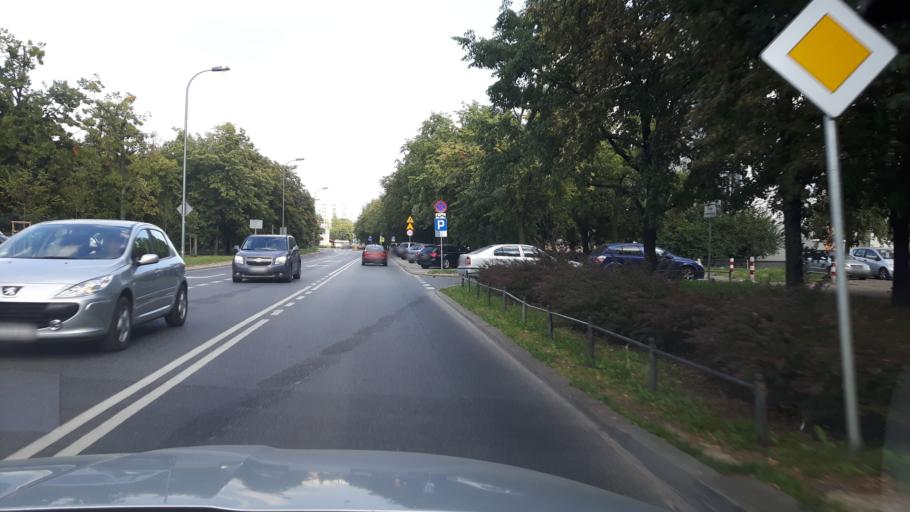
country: PL
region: Masovian Voivodeship
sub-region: Warszawa
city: Targowek
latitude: 52.2963
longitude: 21.0376
